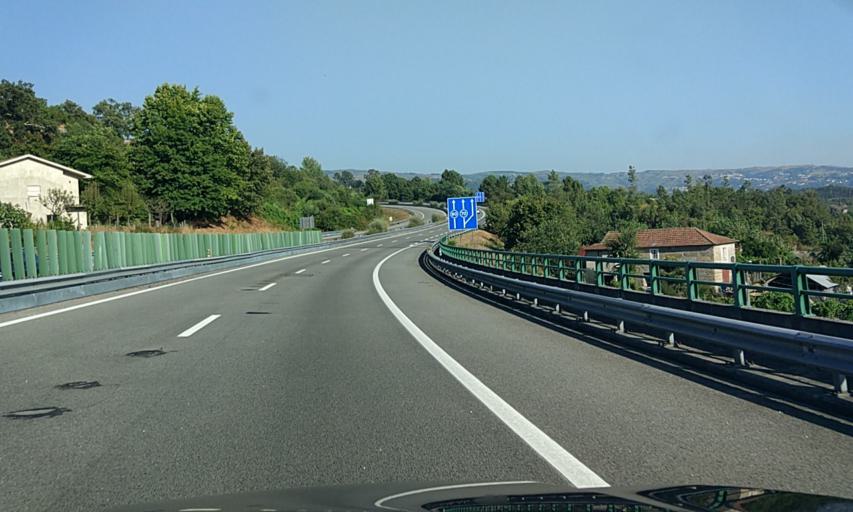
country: PT
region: Porto
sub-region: Marco de Canaveses
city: Marco de Canavezes
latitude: 41.2268
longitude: -8.1585
